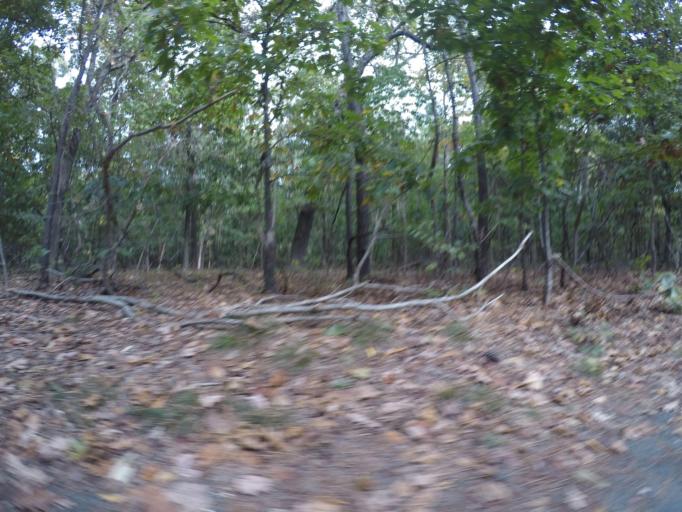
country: US
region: Delaware
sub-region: Sussex County
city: Rehoboth Beach
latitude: 38.7173
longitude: -75.1053
